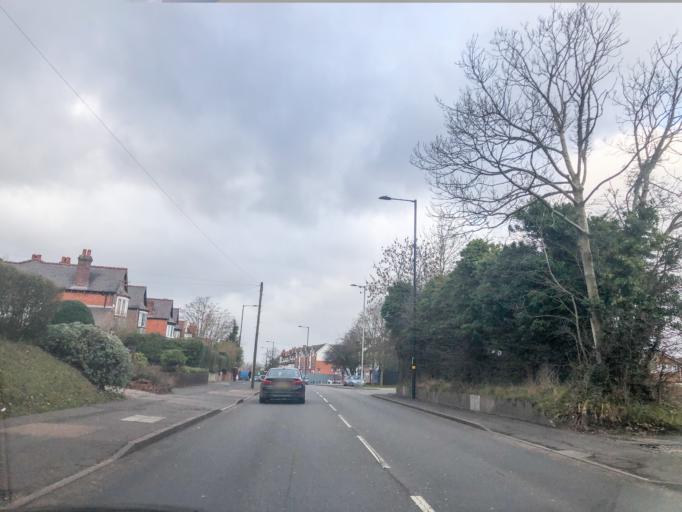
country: GB
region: England
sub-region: Solihull
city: Tidbury Green
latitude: 52.4197
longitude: -1.8915
